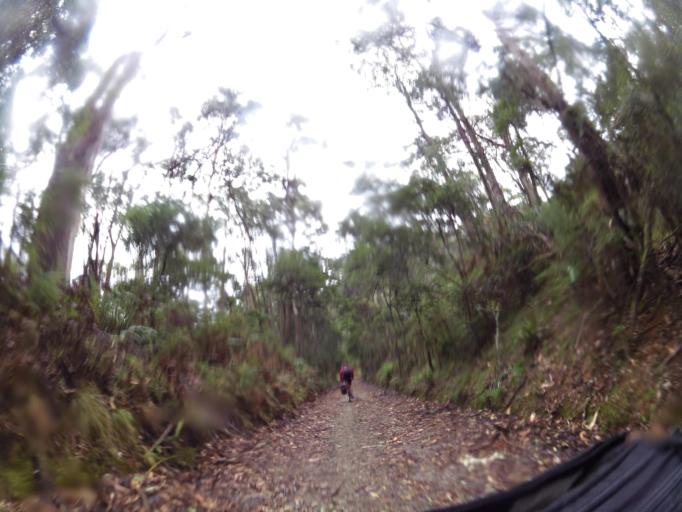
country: AU
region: New South Wales
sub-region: Greater Hume Shire
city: Holbrook
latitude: -36.1946
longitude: 147.5198
